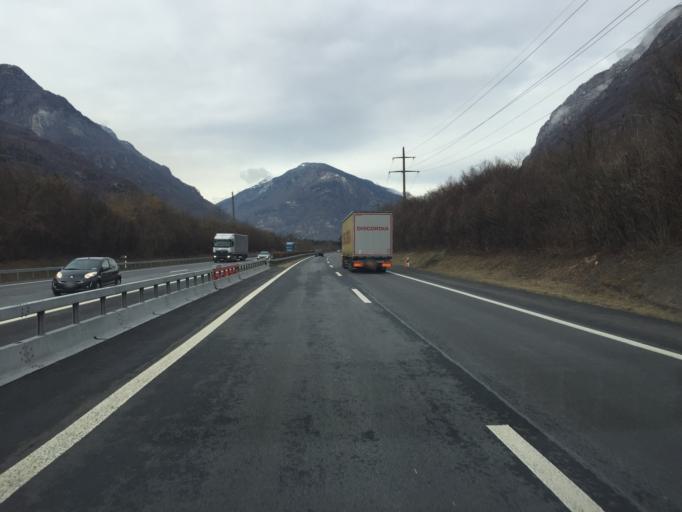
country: CH
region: Ticino
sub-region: Riviera District
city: Lodrino
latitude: 46.3051
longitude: 8.9846
